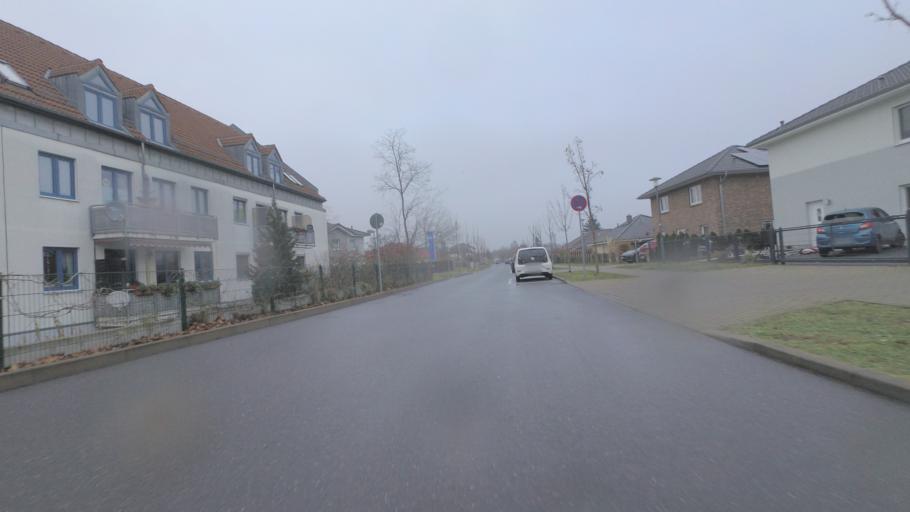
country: DE
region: Brandenburg
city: Grossbeeren
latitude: 52.3513
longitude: 13.3007
